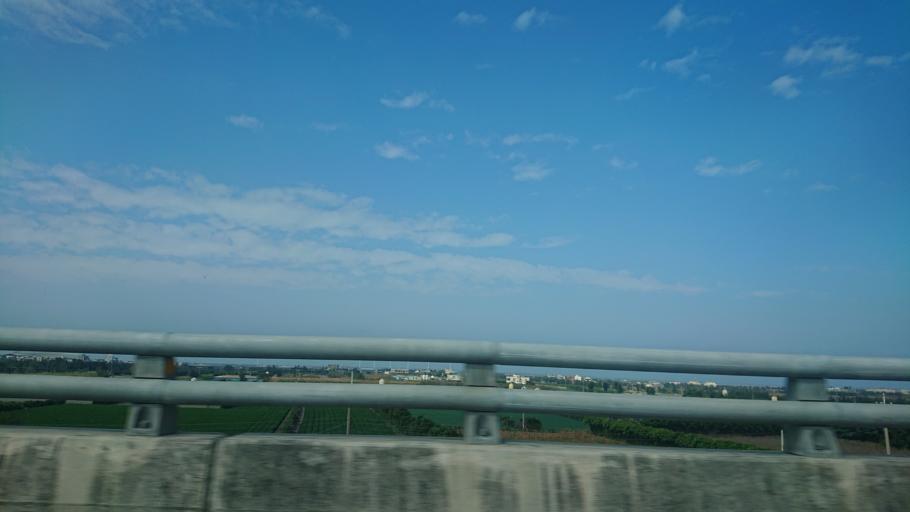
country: TW
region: Taiwan
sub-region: Changhua
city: Chang-hua
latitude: 23.9783
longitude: 120.3629
